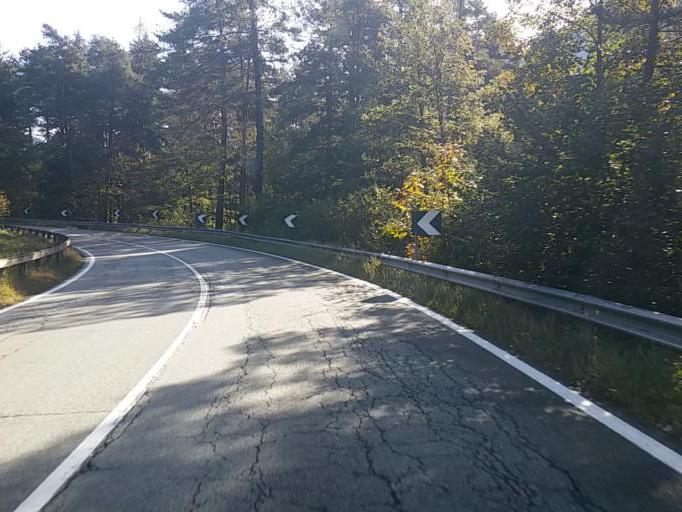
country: IT
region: Piedmont
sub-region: Provincia Verbano-Cusio-Ossola
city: Druogno
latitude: 46.1339
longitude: 8.4408
